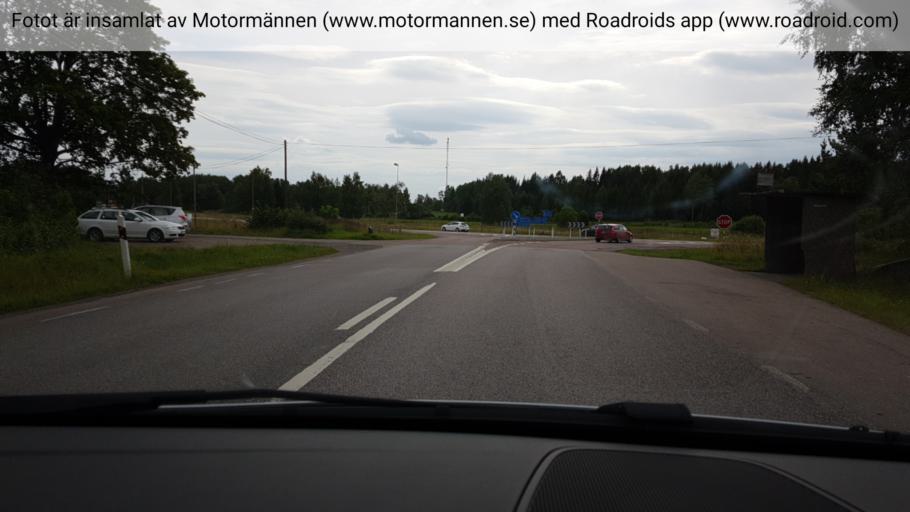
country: SE
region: Uppsala
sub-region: Osthammars Kommun
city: OEsthammar
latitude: 60.2985
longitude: 18.2835
